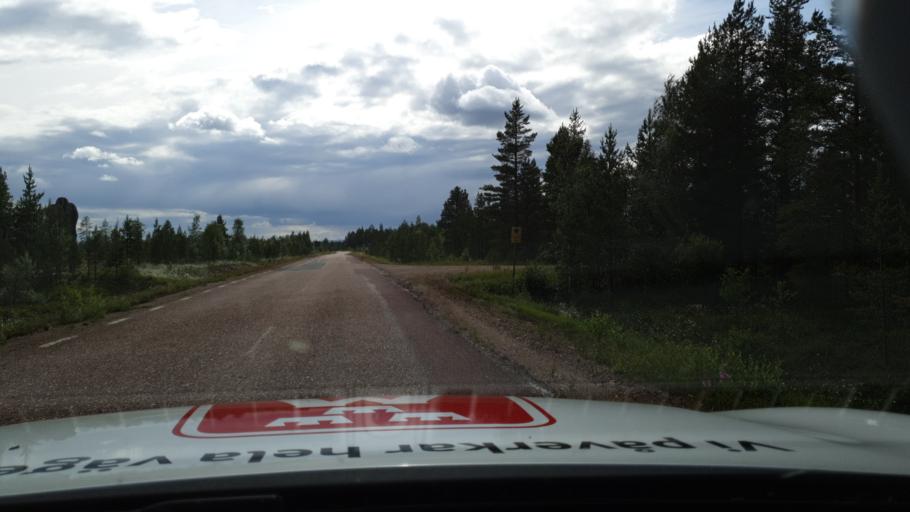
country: SE
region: Dalarna
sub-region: Alvdalens Kommun
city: AElvdalen
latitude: 61.7617
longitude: 13.4639
